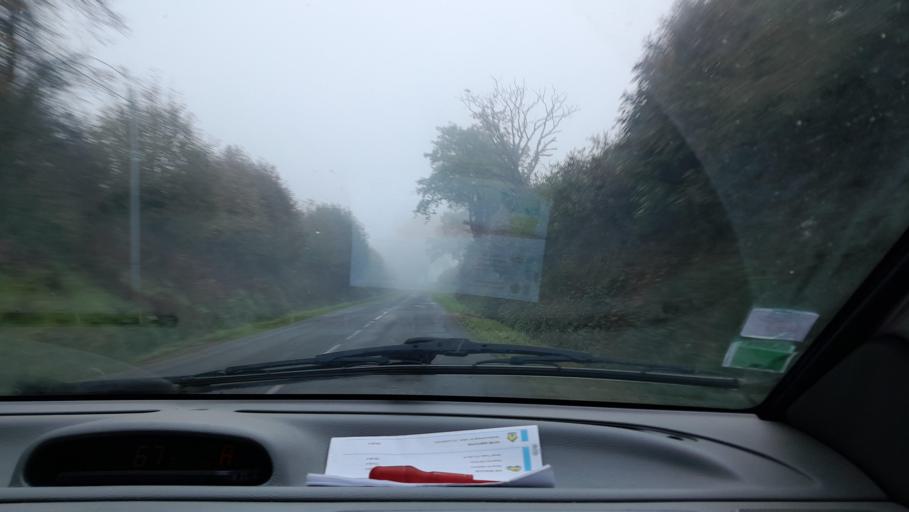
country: FR
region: Brittany
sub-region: Departement d'Ille-et-Vilaine
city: Le Pertre
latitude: 48.0401
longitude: -1.0357
